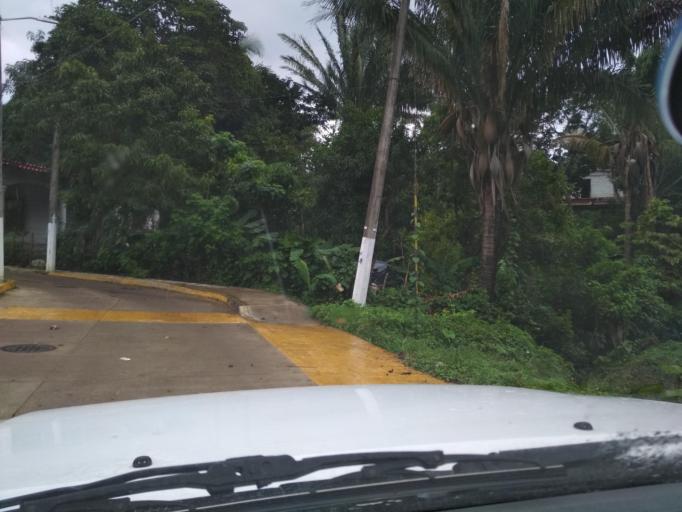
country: MX
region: Veracruz
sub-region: San Andres Tuxtla
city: San Isidro Xoteapan (San Isidro Texcaltitan)
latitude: 18.4591
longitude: -95.2335
